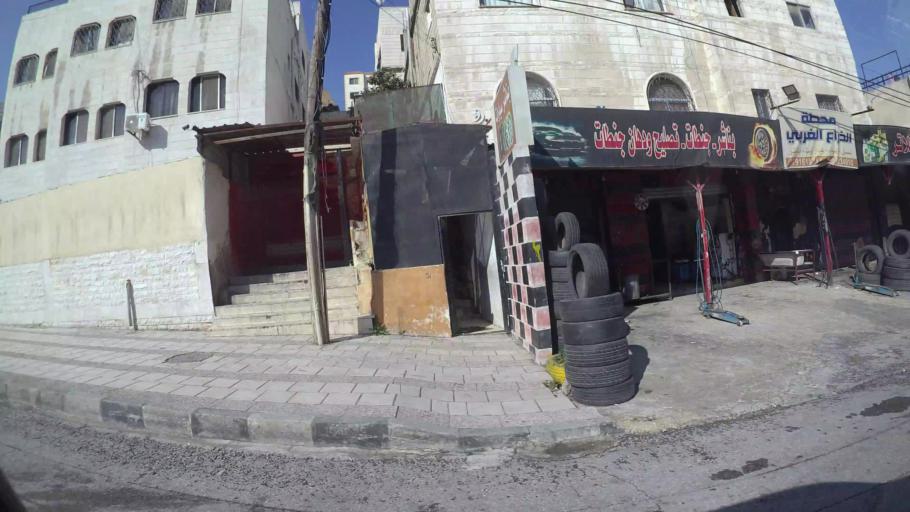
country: JO
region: Amman
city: Amman
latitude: 31.9365
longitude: 35.9093
